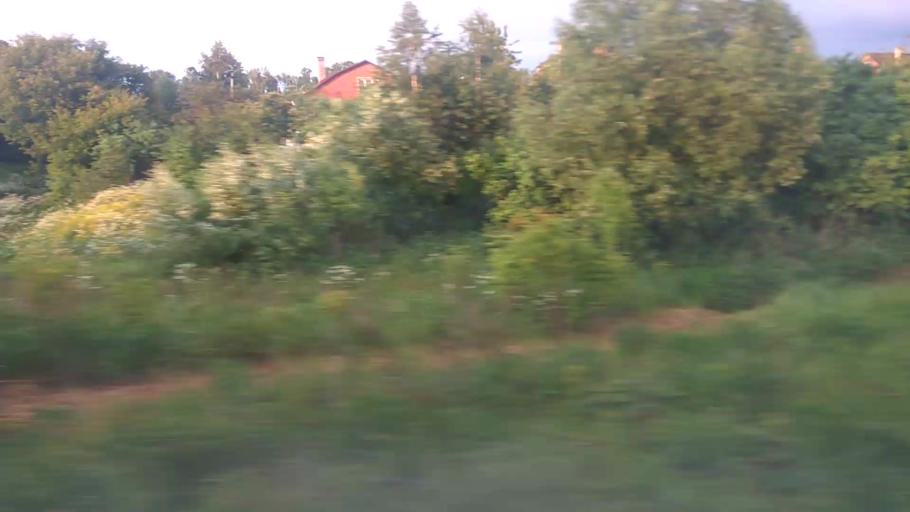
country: RU
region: Moskovskaya
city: Stupino
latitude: 54.8895
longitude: 38.0961
